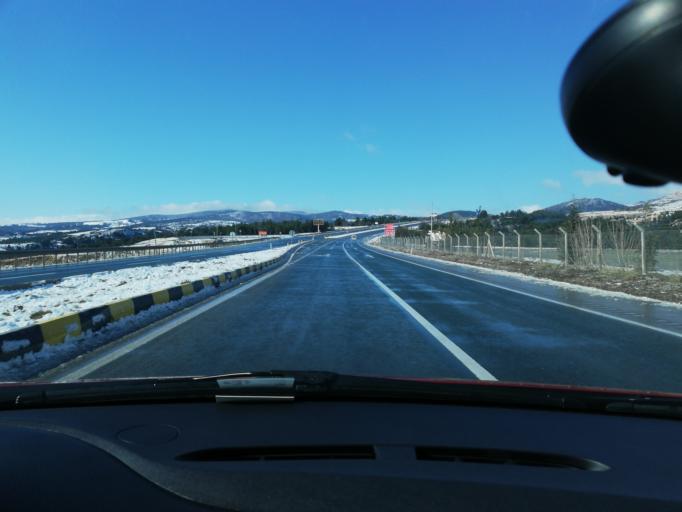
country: TR
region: Kastamonu
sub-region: Cide
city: Kastamonu
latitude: 41.3656
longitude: 33.7415
